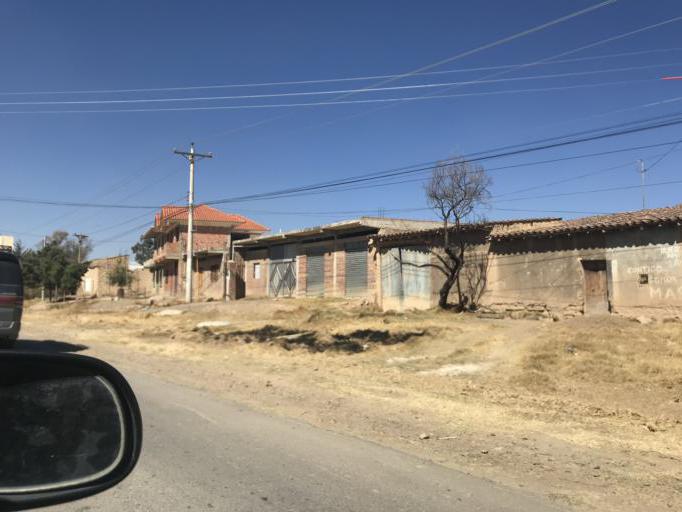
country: BO
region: Cochabamba
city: Cliza
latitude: -17.5977
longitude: -65.9571
